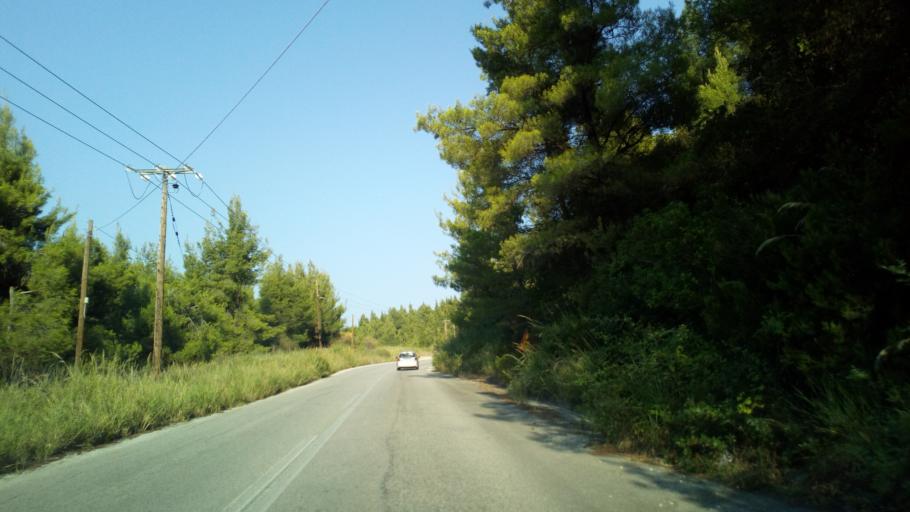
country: GR
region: Central Macedonia
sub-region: Nomos Chalkidikis
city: Neos Marmaras
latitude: 40.1772
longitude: 23.8331
